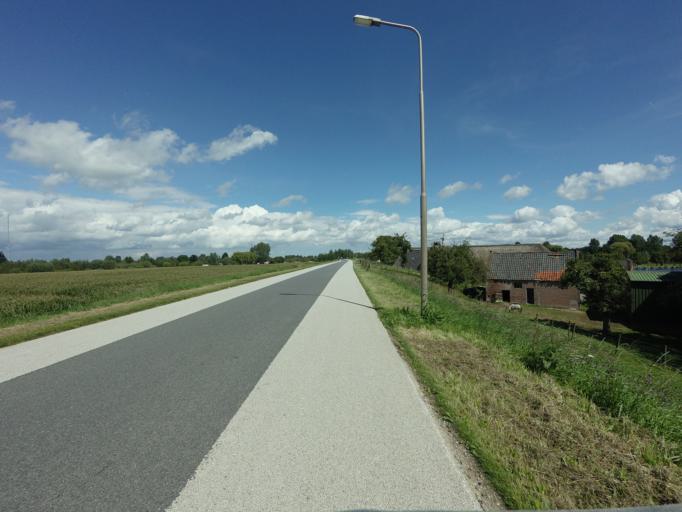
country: NL
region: Utrecht
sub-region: Gemeente Lopik
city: Lopik
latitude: 51.9565
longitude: 4.9386
